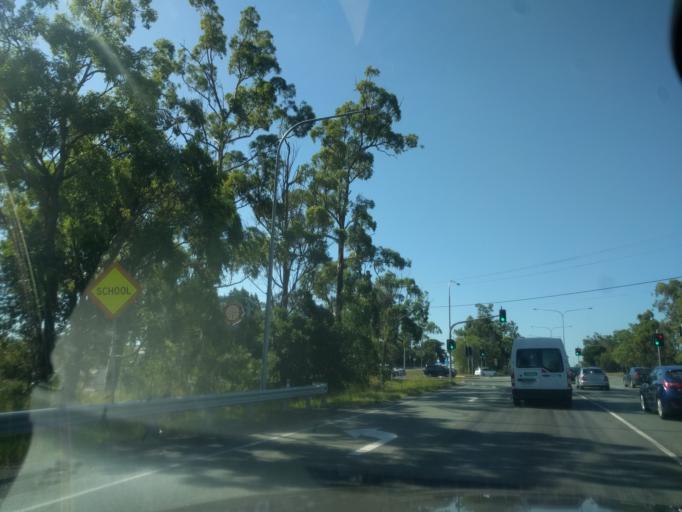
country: AU
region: Queensland
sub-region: Brisbane
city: Sunnybank Hills
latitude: -27.6310
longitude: 153.0466
